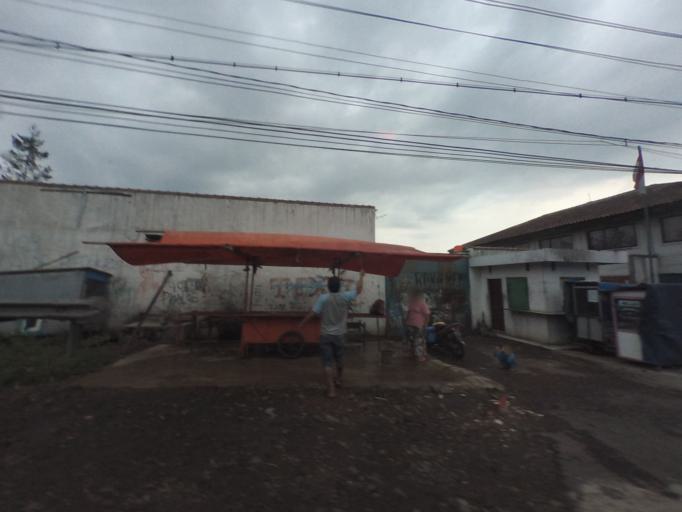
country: ID
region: West Java
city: Cicurug
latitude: -6.8435
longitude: 106.7617
